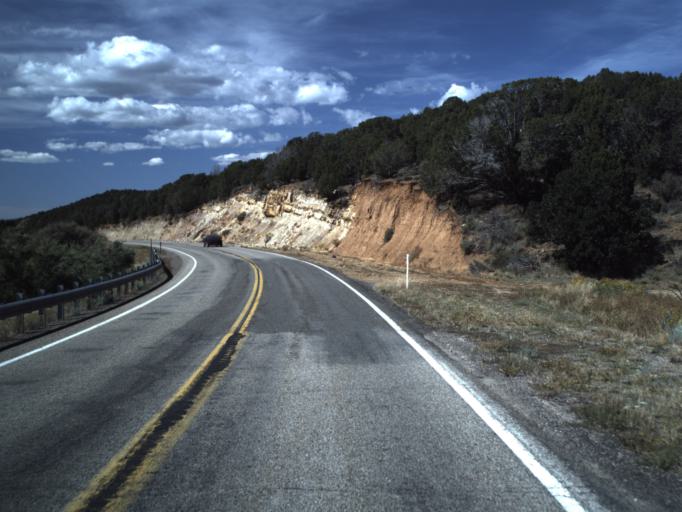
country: US
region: Utah
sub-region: Washington County
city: Enterprise
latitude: 37.5392
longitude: -113.6564
